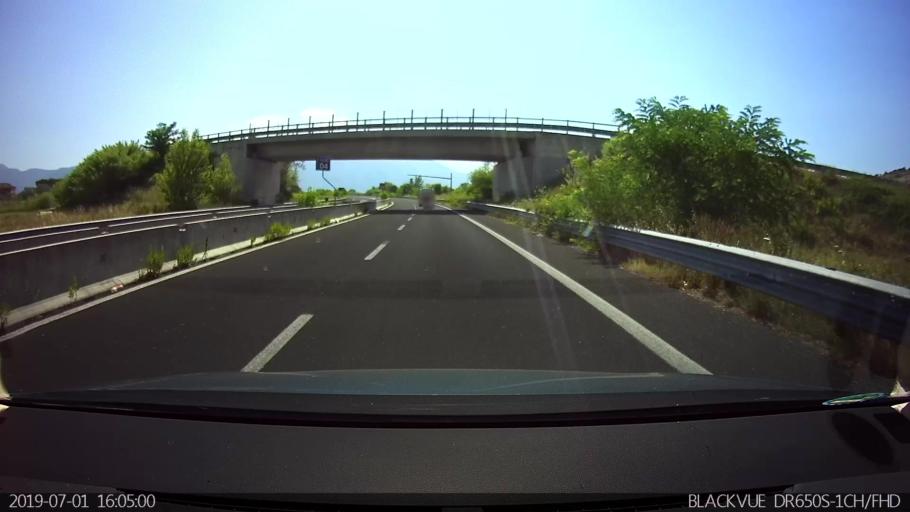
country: IT
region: Latium
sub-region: Provincia di Frosinone
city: Monte San Marino
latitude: 41.6719
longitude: 13.3012
